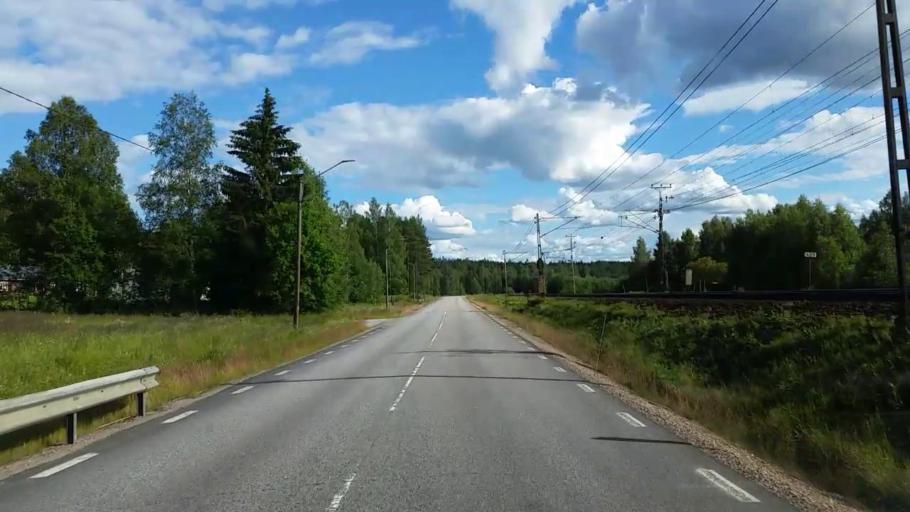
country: SE
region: Vaesternorrland
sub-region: Ange Kommun
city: Ange
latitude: 62.1684
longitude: 15.6754
